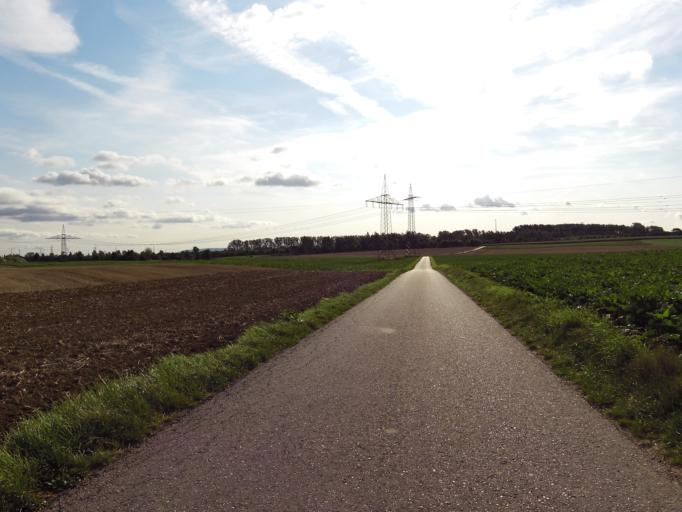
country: DE
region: North Rhine-Westphalia
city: Siersdorf
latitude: 50.9072
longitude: 6.2113
